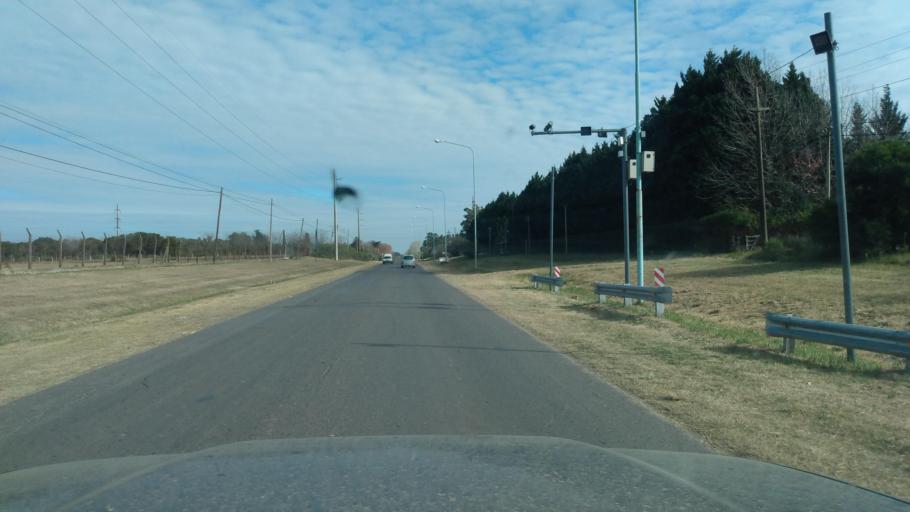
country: AR
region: Buenos Aires
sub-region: Partido de Lujan
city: Lujan
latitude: -34.5694
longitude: -59.1513
